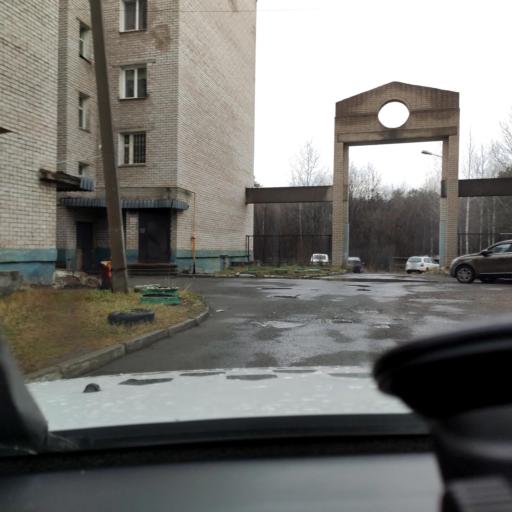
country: RU
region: Perm
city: Perm
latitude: 58.0569
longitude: 56.2808
